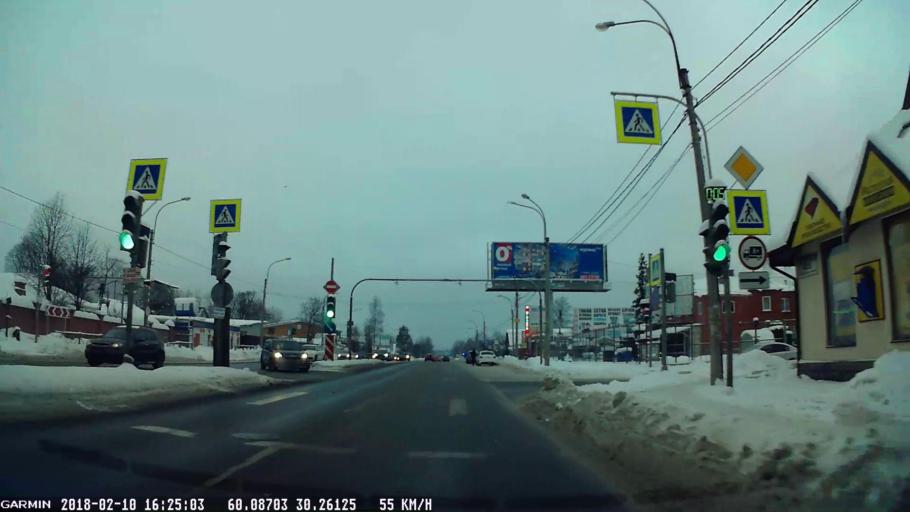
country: RU
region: St.-Petersburg
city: Pargolovo
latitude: 60.0879
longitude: 30.2606
